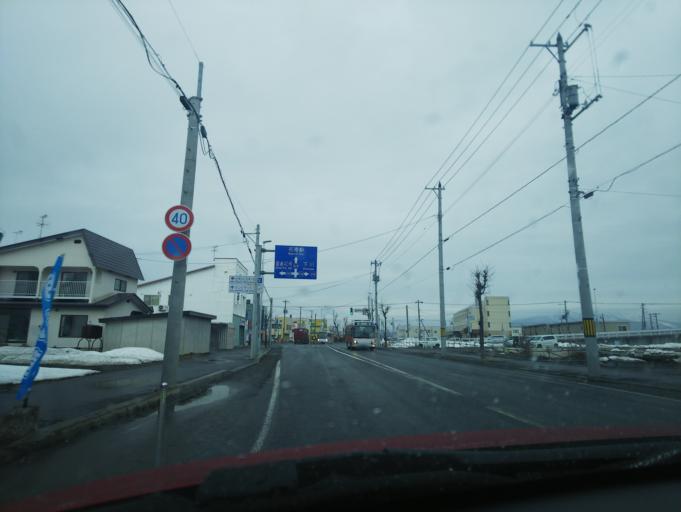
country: JP
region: Hokkaido
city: Nayoro
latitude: 44.3456
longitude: 142.4641
